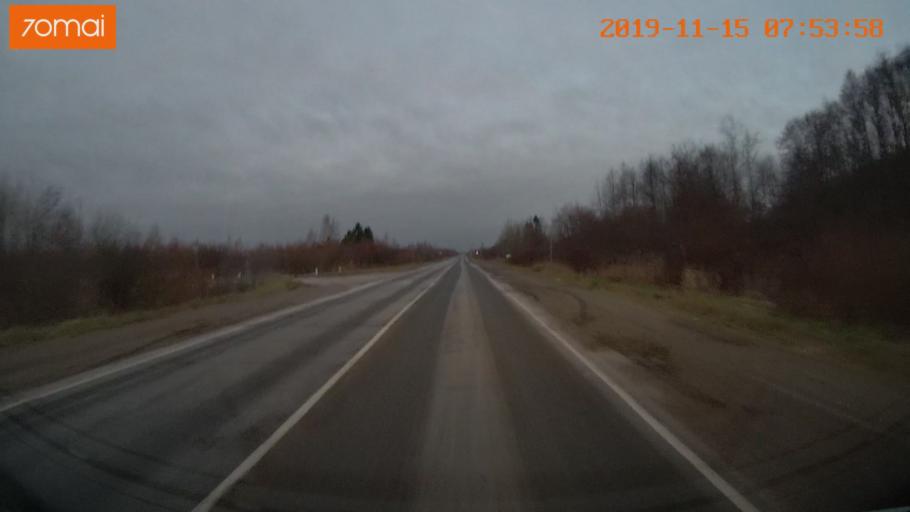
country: RU
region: Vologda
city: Cherepovets
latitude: 58.8940
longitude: 38.1814
